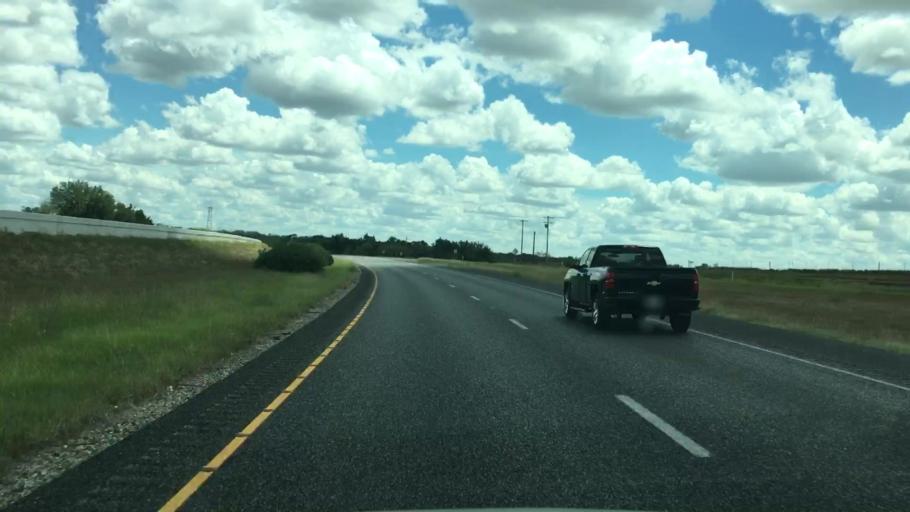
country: US
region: Texas
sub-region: Atascosa County
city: Pleasanton
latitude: 28.9084
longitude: -98.4330
